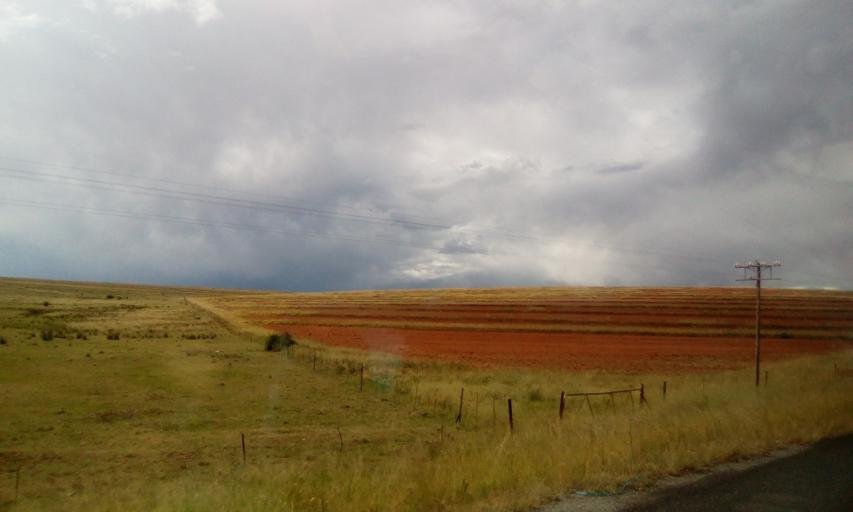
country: ZA
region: Orange Free State
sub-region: Thabo Mofutsanyana District Municipality
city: Ladybrand
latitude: -29.2278
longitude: 27.4518
